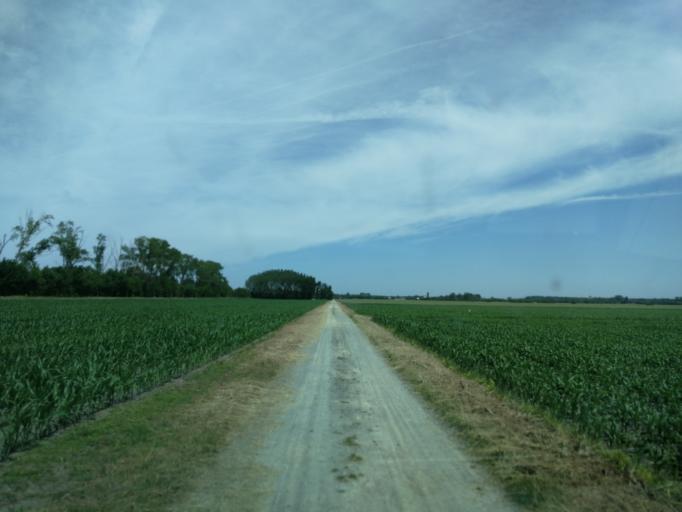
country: FR
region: Pays de la Loire
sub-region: Departement de la Vendee
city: Le Langon
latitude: 46.3702
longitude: -0.9572
